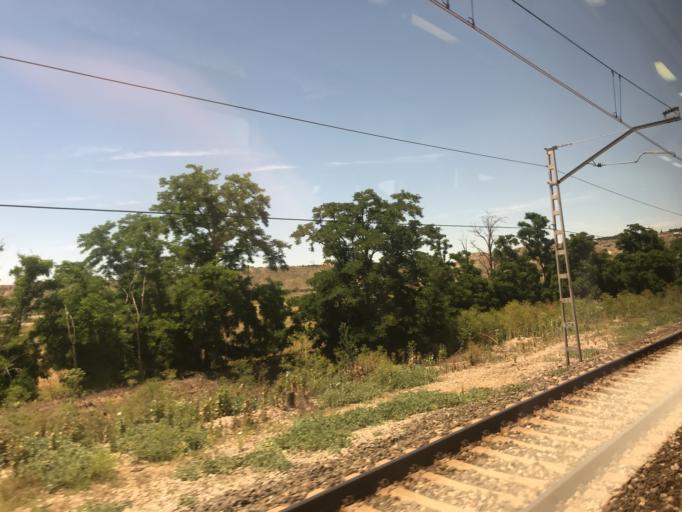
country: ES
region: Madrid
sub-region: Provincia de Madrid
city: Aranjuez
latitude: 40.0589
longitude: -3.6359
